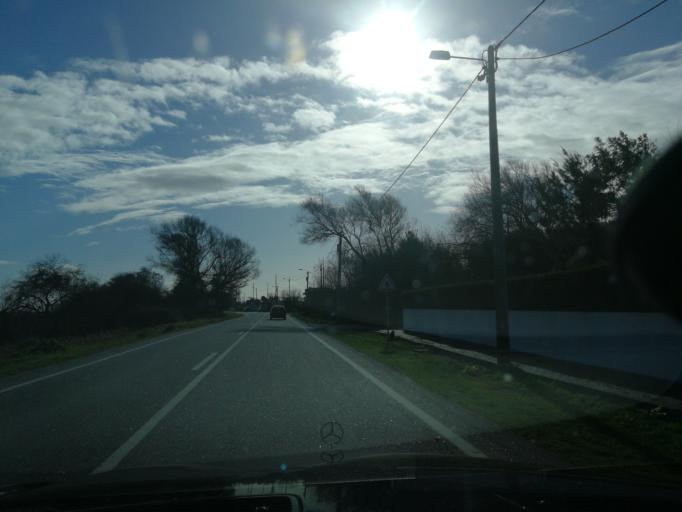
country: PT
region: Aveiro
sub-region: Estarreja
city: Pardilho
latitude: 40.8206
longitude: -8.6691
